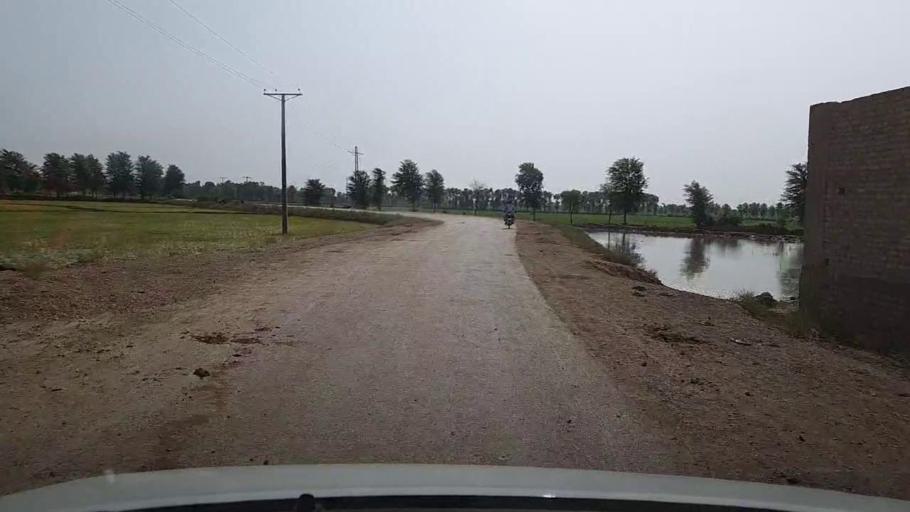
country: PK
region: Sindh
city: Mehar
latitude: 27.1215
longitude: 67.8547
